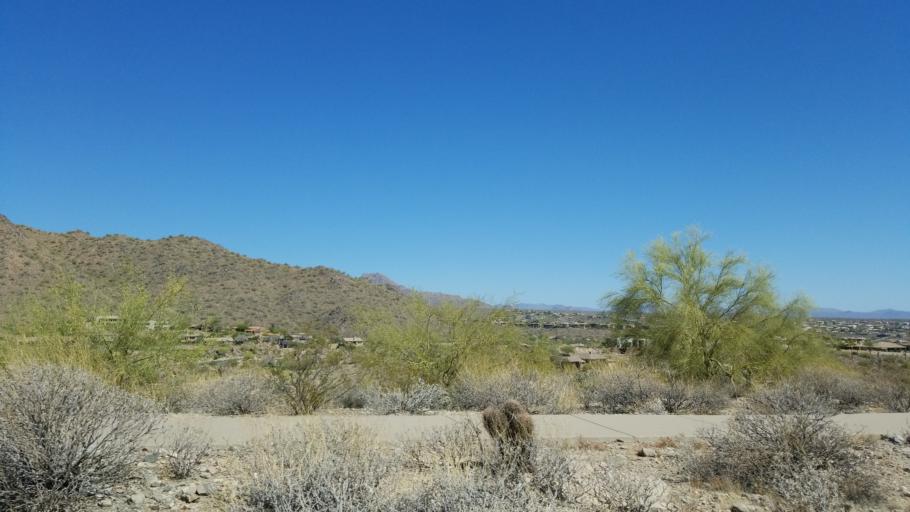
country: US
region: Arizona
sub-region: Maricopa County
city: Fountain Hills
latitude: 33.6051
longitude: -111.7496
